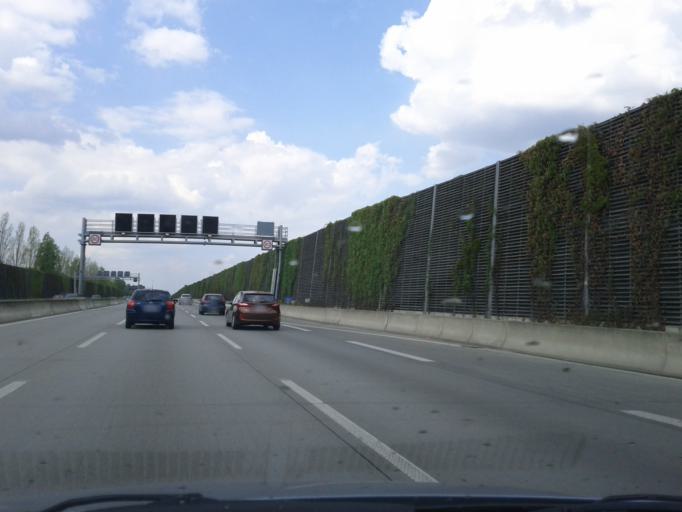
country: DE
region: Berlin
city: Rudow
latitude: 52.4364
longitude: 13.4931
